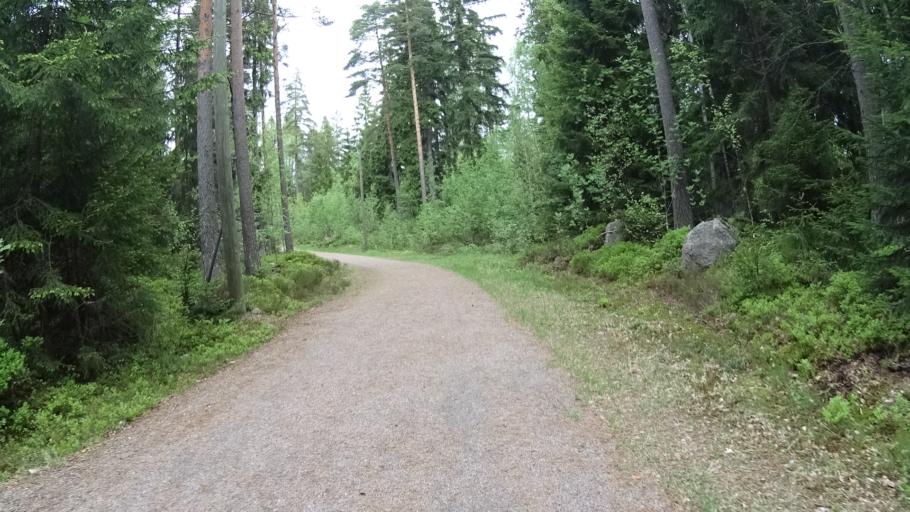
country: FI
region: Uusimaa
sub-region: Helsinki
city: Espoo
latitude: 60.2334
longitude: 24.6839
